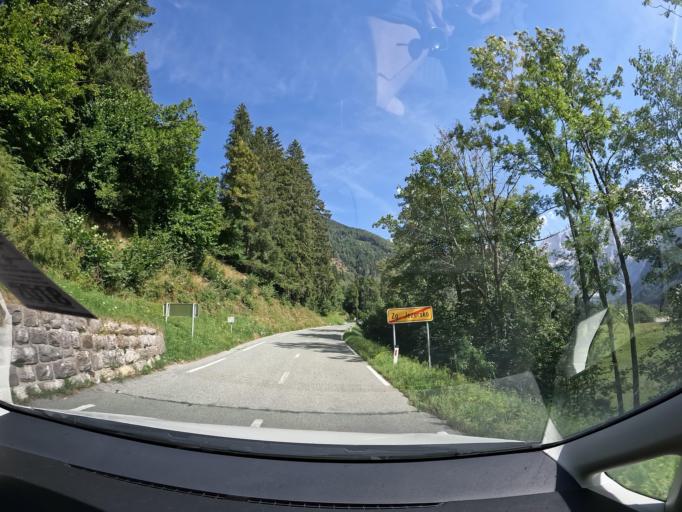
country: AT
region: Carinthia
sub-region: Politischer Bezirk Feldkirchen
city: Glanegg
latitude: 46.7143
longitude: 14.1610
